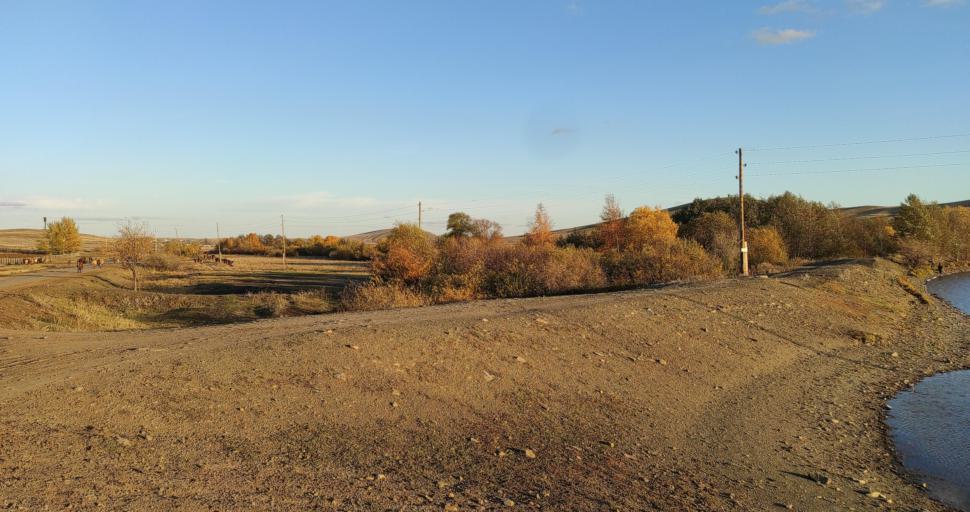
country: RU
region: Bashkortostan
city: Sibay
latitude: 52.8799
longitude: 58.4846
